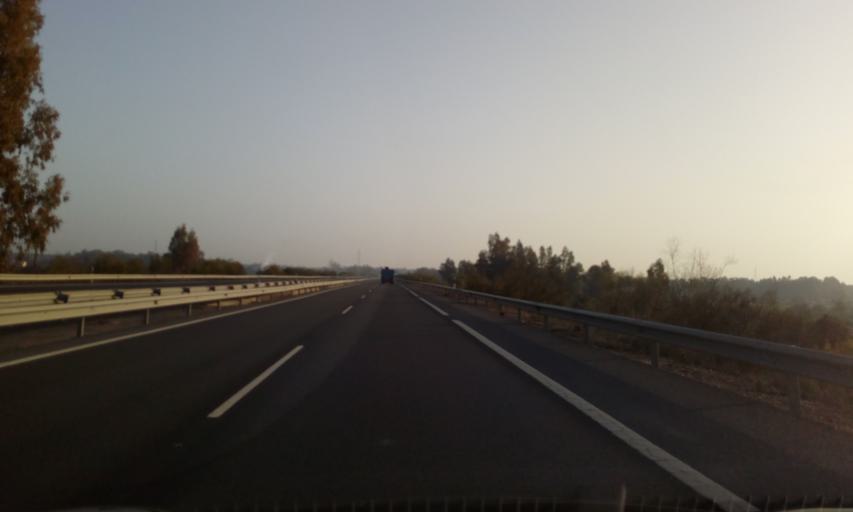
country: ES
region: Andalusia
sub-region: Provincia de Huelva
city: Gibraleon
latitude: 37.3506
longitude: -6.9846
